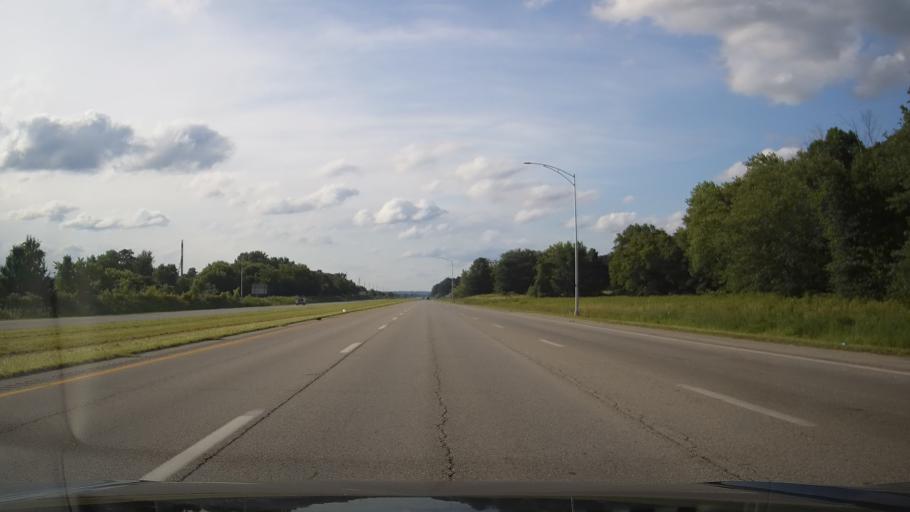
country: US
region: Ohio
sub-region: Scioto County
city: Franklin Furnace
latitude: 38.6519
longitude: -82.8516
